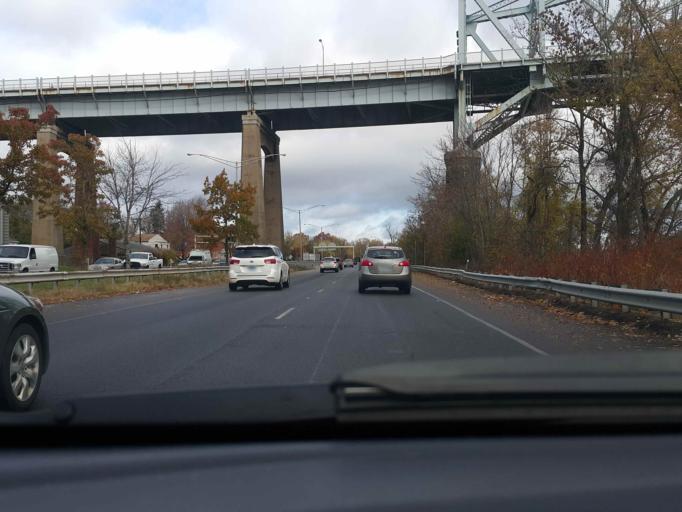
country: US
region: Connecticut
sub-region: Middlesex County
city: Middletown
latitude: 41.5681
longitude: -72.6506
